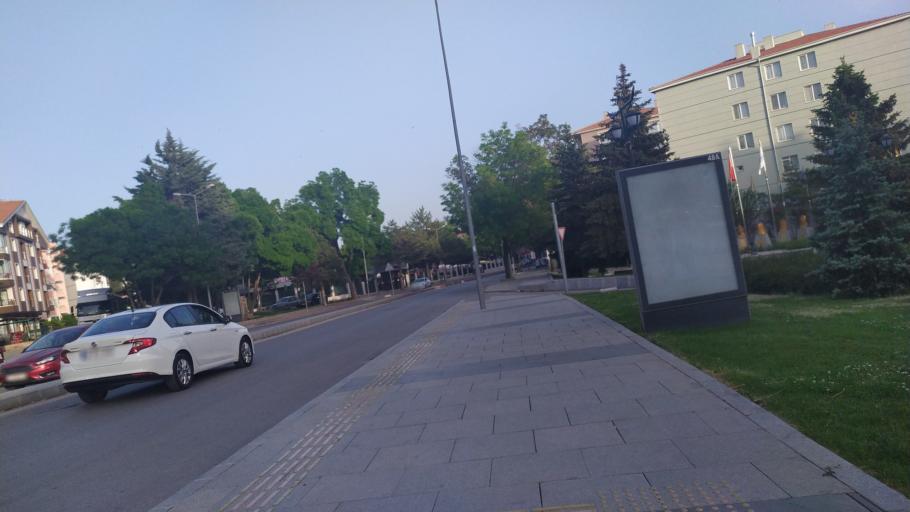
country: TR
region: Kirsehir
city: Kirsehir
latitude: 39.1544
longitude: 34.1596
